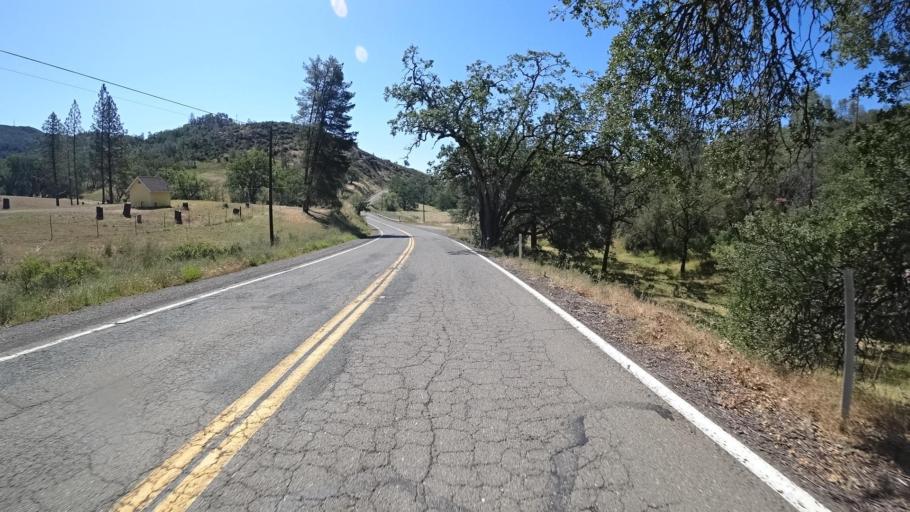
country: US
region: California
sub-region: Lake County
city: Lower Lake
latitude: 38.8864
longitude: -122.5345
